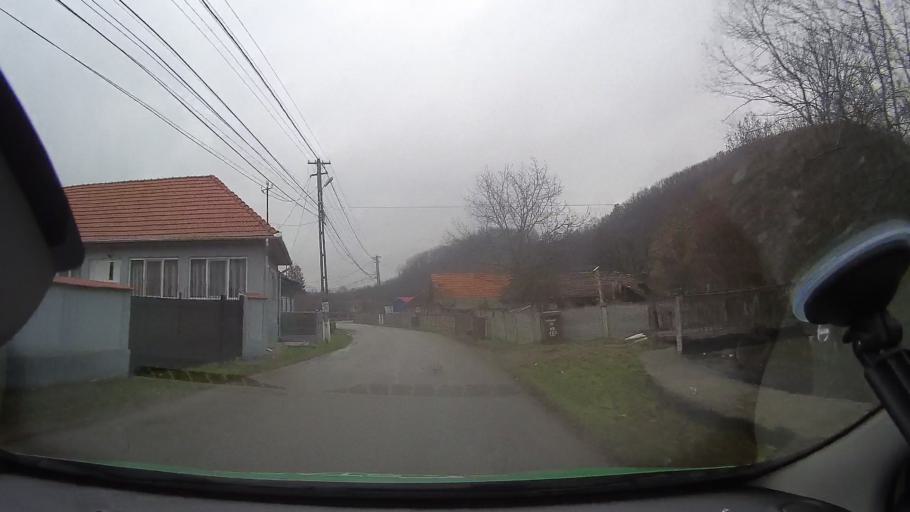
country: RO
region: Arad
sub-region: Comuna Halmagel
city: Halmagel
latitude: 46.2691
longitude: 22.6195
